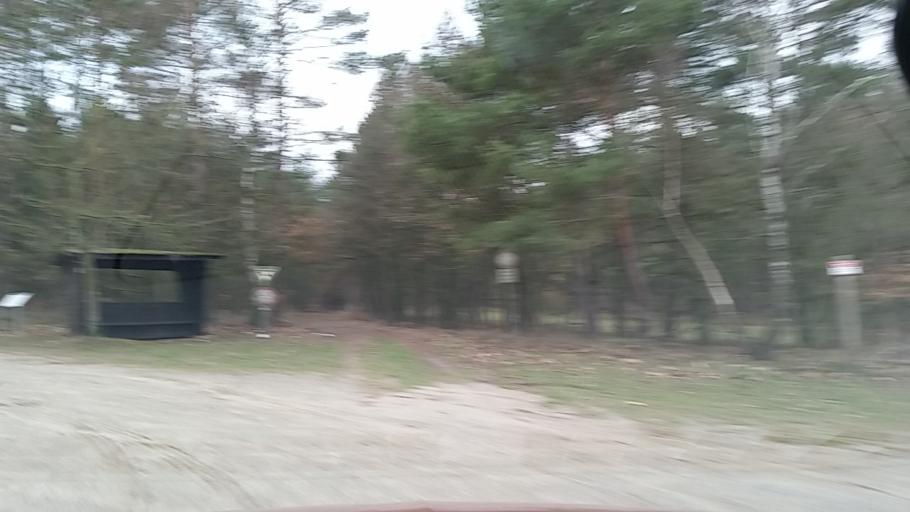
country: DE
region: Lower Saxony
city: Bodenteich
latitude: 52.8508
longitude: 10.6594
